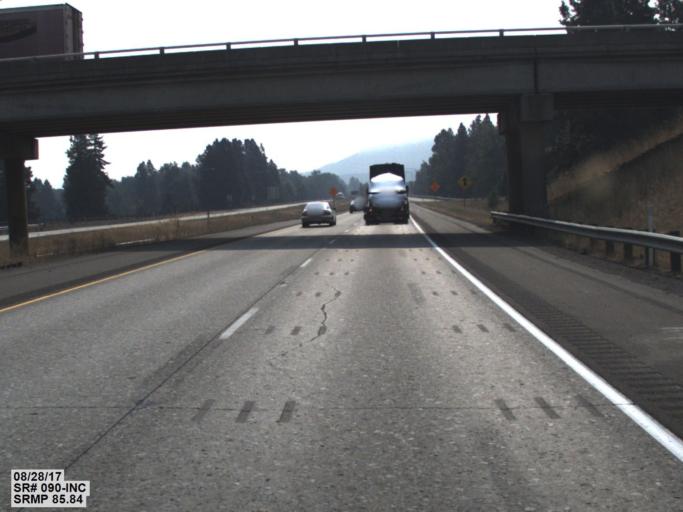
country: US
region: Washington
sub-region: Kittitas County
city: Cle Elum
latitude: 47.1834
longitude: -120.9035
